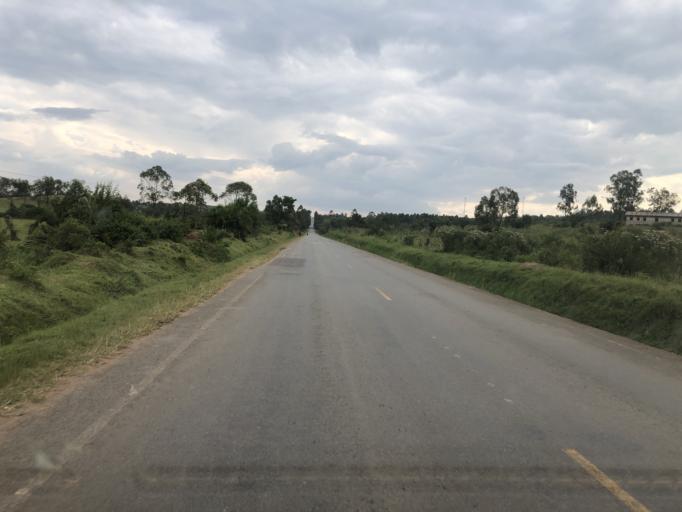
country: UG
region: Western Region
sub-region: Sheema District
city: Kibingo
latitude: -0.5792
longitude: 30.4198
